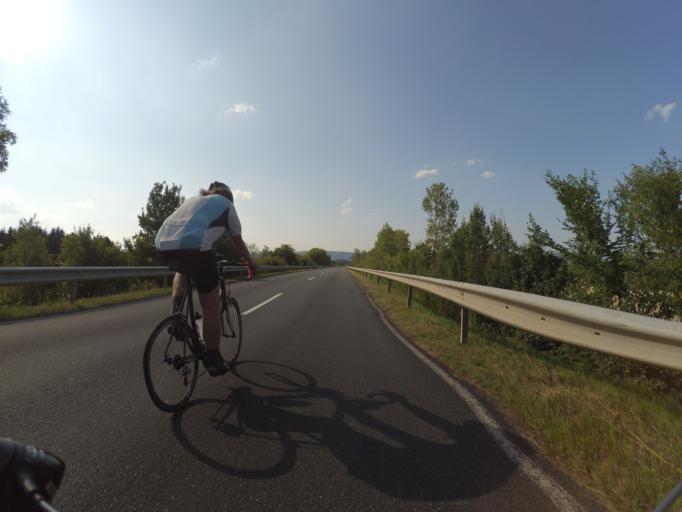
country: DE
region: Rheinland-Pfalz
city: Minheim
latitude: 49.8535
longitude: 6.9642
